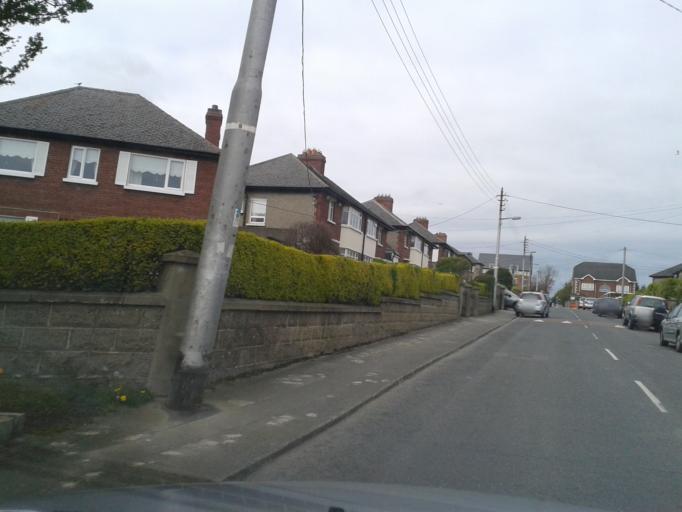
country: IE
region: Leinster
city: Marino
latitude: 53.3736
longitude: -6.2385
